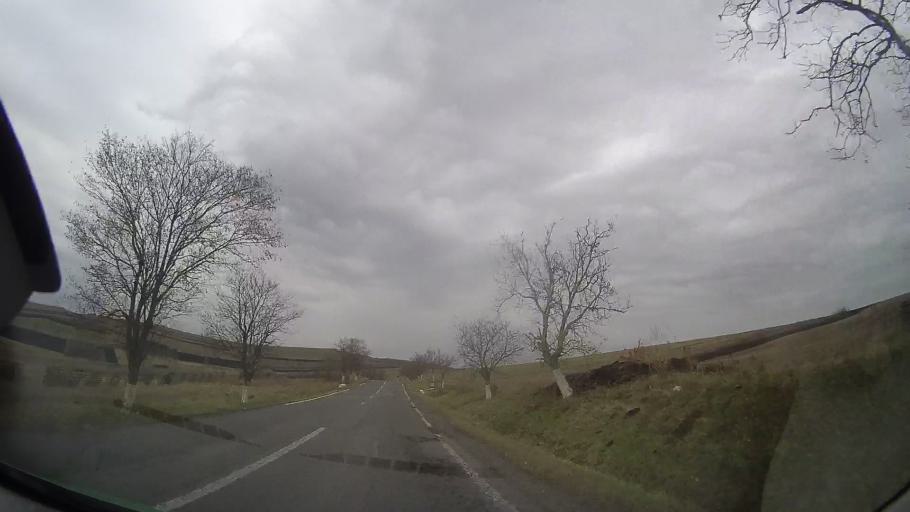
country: RO
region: Mures
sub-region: Comuna Faragau
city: Faragau
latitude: 46.7610
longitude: 24.5310
